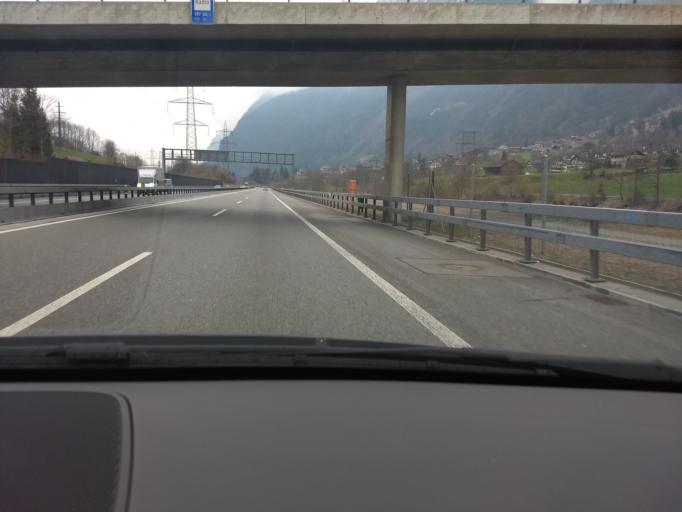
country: CH
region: Uri
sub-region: Uri
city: Silenen
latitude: 46.7944
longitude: 8.6651
